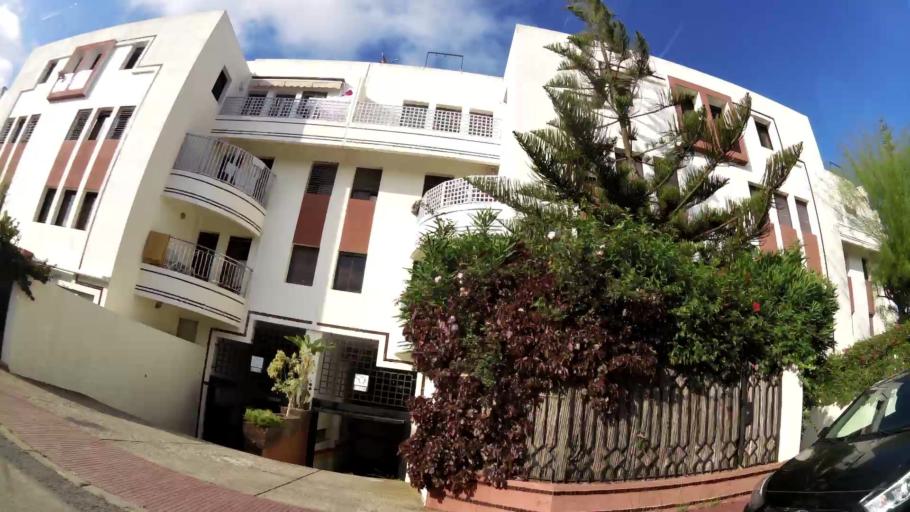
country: MA
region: Rabat-Sale-Zemmour-Zaer
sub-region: Skhirate-Temara
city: Temara
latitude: 33.9570
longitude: -6.8582
